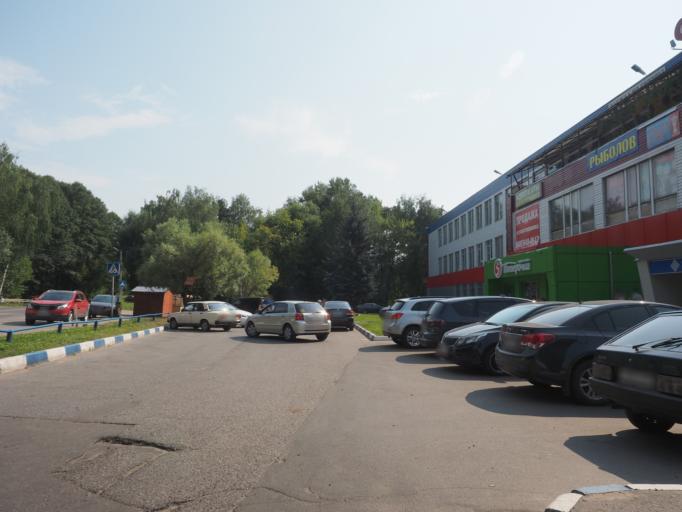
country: RU
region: Moskovskaya
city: Udel'naya
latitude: 55.6354
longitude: 38.0105
